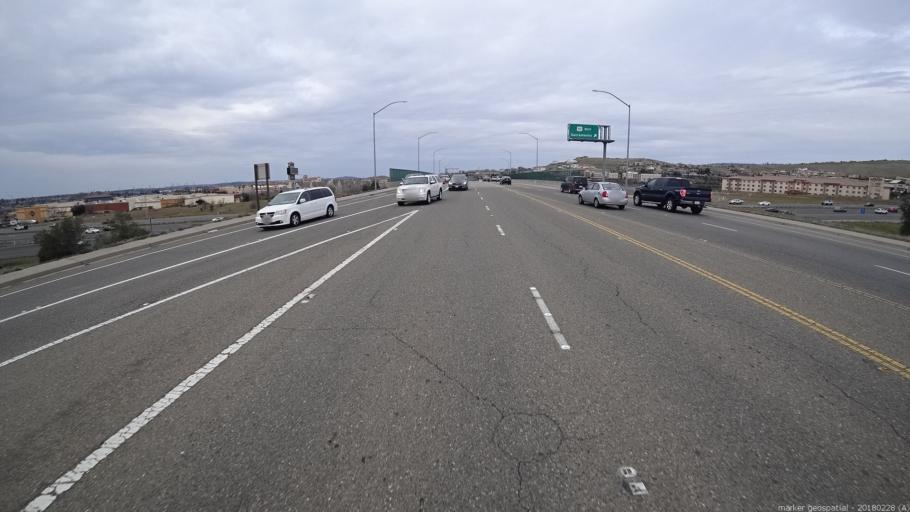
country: US
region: California
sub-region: El Dorado County
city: El Dorado Hills
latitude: 38.6424
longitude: -121.1149
